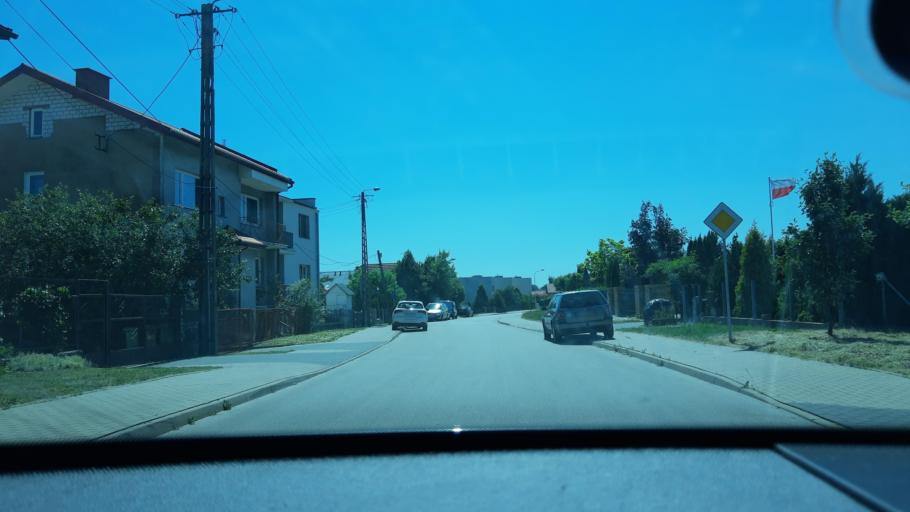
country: PL
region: Lodz Voivodeship
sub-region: Powiat sieradzki
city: Sieradz
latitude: 51.5834
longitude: 18.7394
